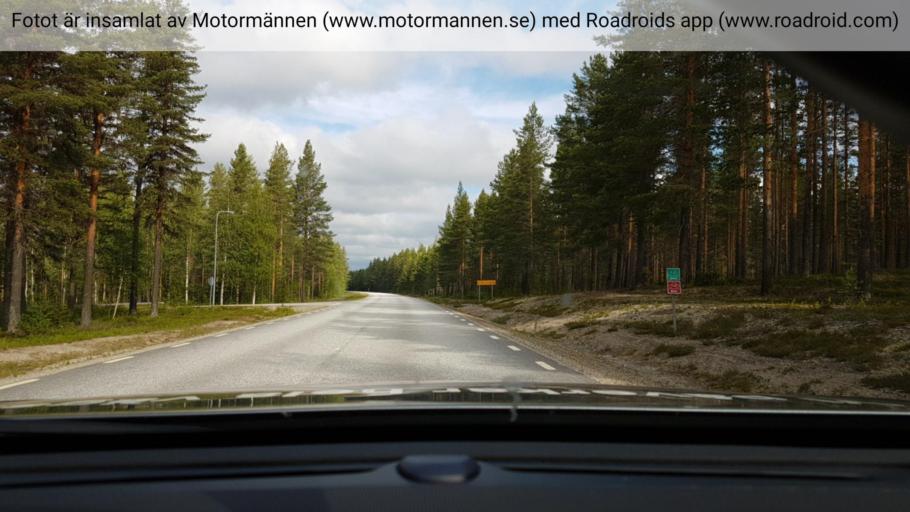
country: SE
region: Vaesterbotten
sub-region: Vindelns Kommun
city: Vindeln
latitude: 64.3686
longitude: 19.4273
